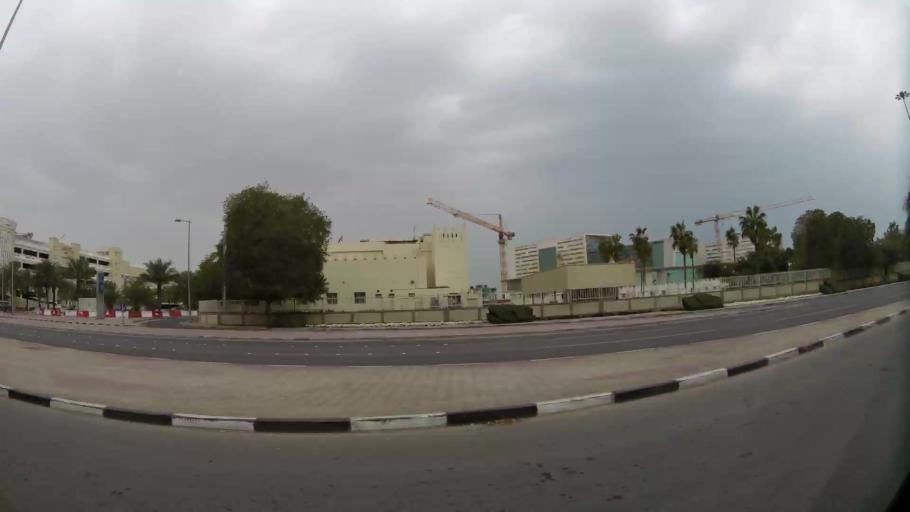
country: QA
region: Baladiyat ad Dawhah
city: Doha
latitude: 25.2909
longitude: 51.5050
